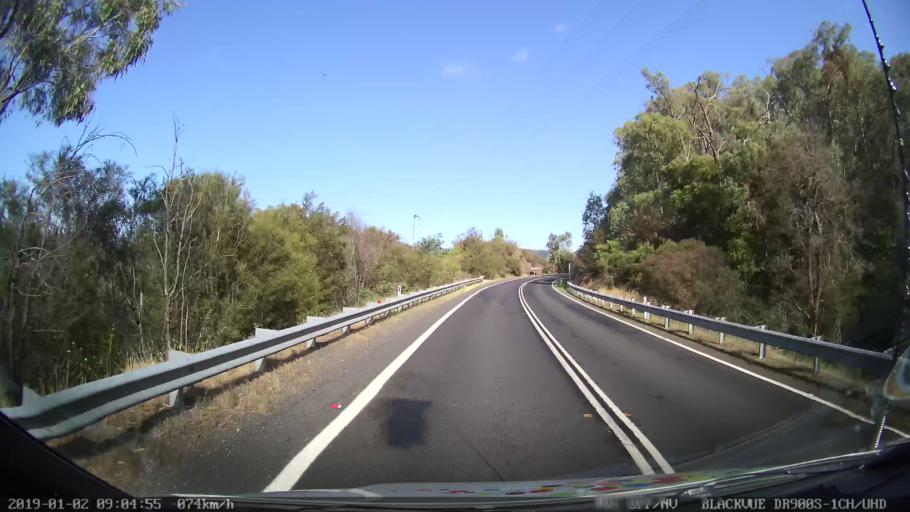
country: AU
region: New South Wales
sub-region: Tumut Shire
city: Tumut
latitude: -35.5642
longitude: 148.3143
